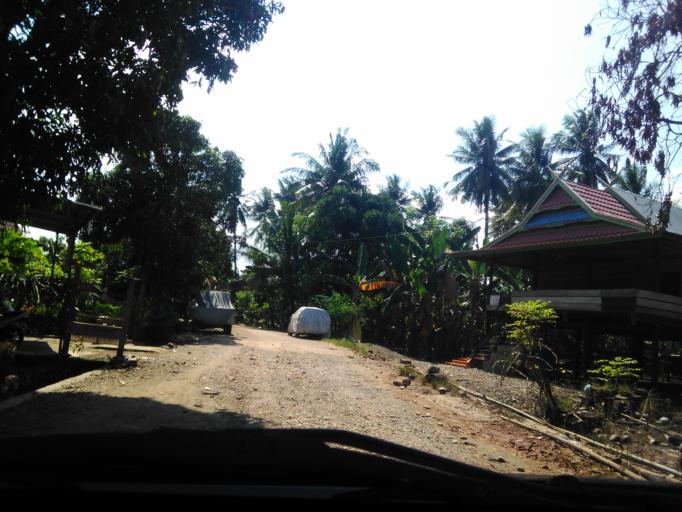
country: ID
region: South Sulawesi
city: Tancung
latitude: -4.0140
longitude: 119.9261
